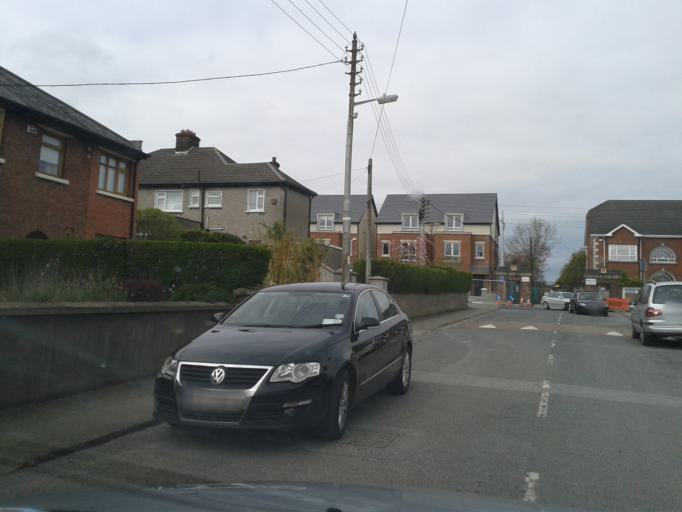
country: IE
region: Leinster
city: Marino
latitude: 53.3745
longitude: -6.2380
